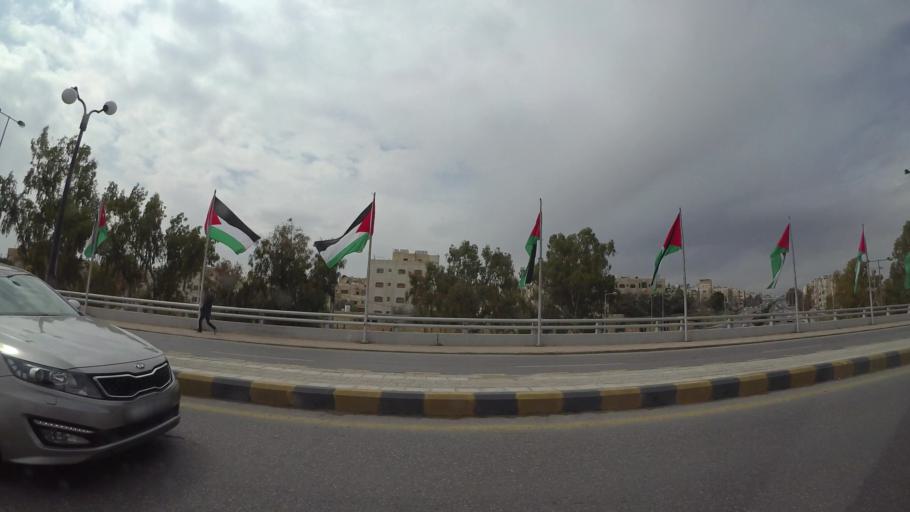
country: JO
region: Amman
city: Amman
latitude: 31.9735
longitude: 35.9350
